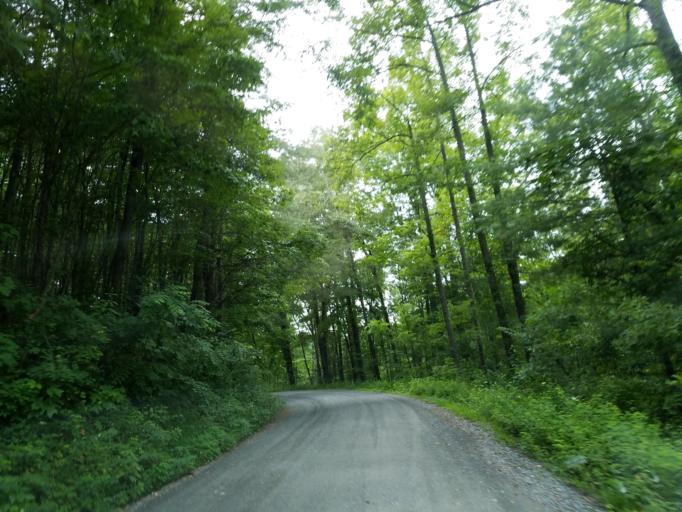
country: US
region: Georgia
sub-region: Fannin County
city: Blue Ridge
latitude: 34.8263
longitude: -84.2301
